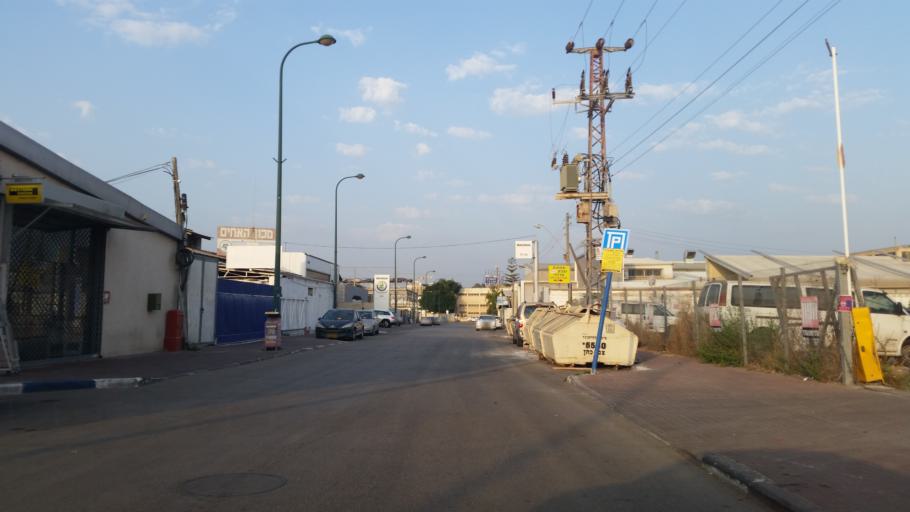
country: IL
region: Central District
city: Bet Yizhaq
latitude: 32.3187
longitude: 34.8739
